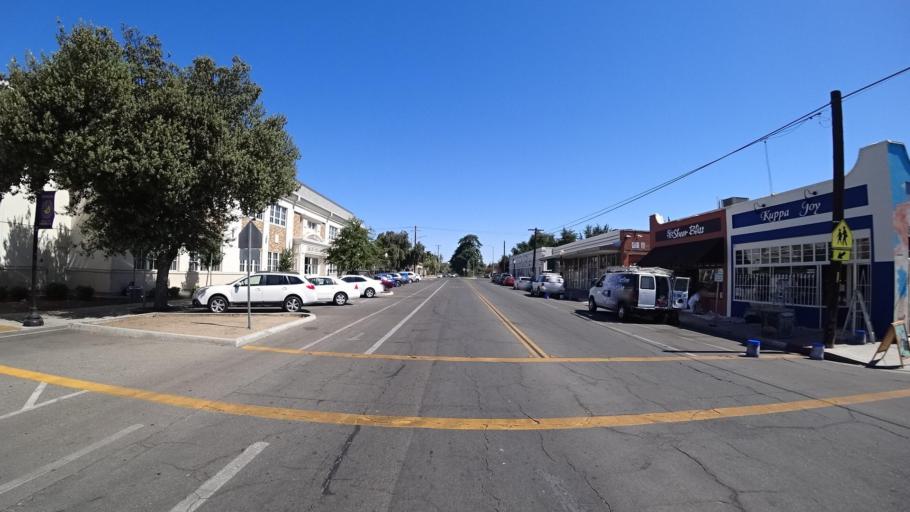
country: US
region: California
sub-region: Fresno County
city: Fresno
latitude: 36.7677
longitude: -119.8042
